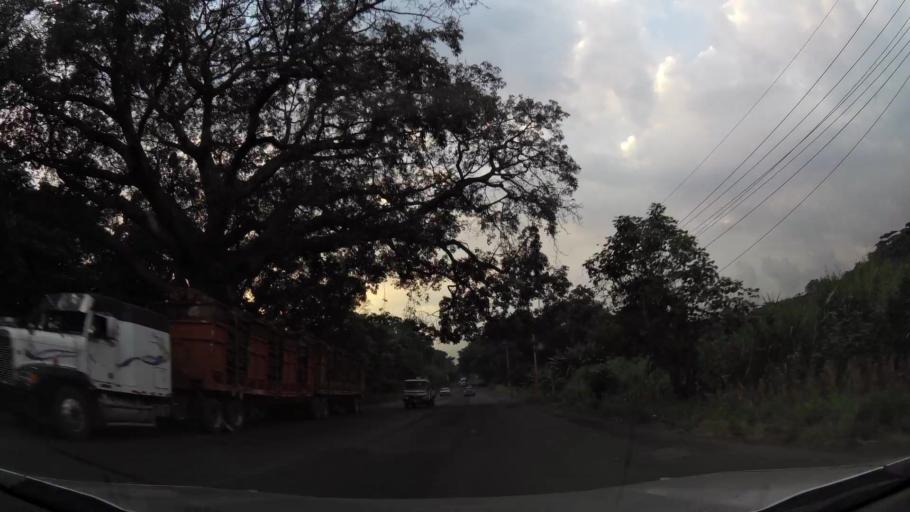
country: GT
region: Escuintla
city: Siquinala
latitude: 14.2832
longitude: -90.9314
